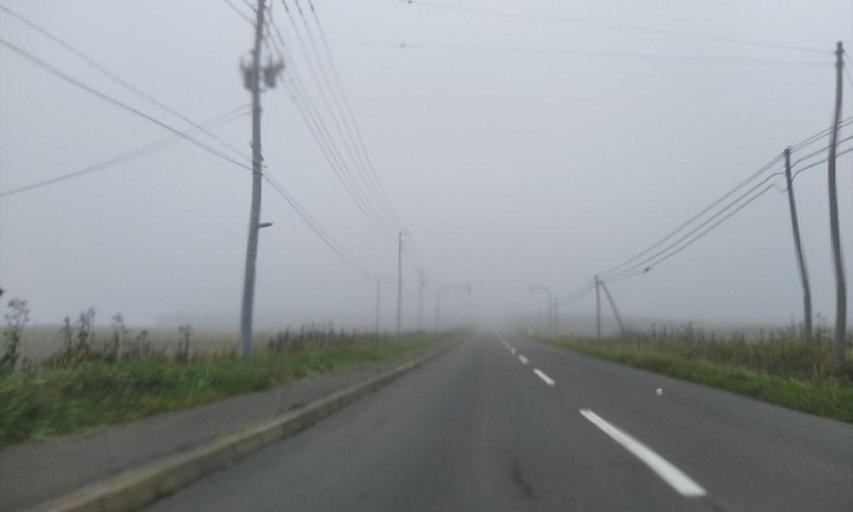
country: JP
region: Hokkaido
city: Nemuro
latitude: 43.3355
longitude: 145.7051
